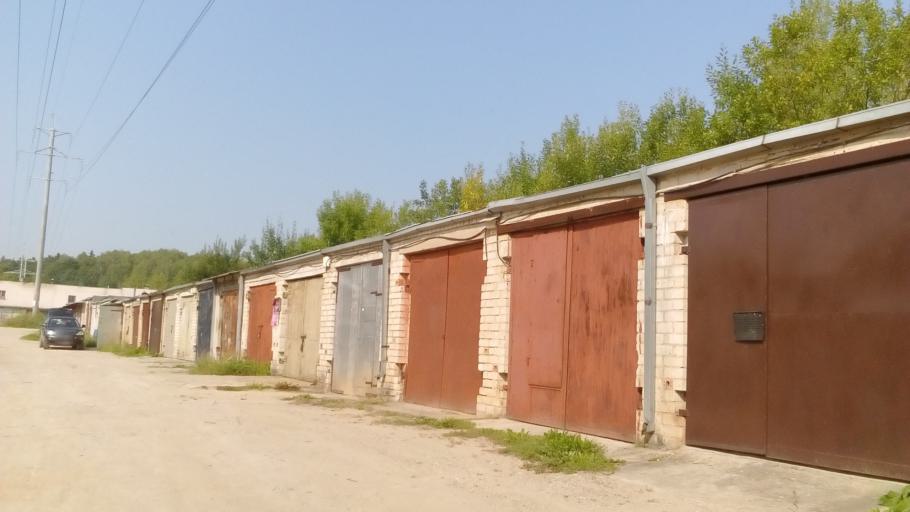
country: LT
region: Alytaus apskritis
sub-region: Alytus
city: Alytus
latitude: 54.3887
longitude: 24.0169
